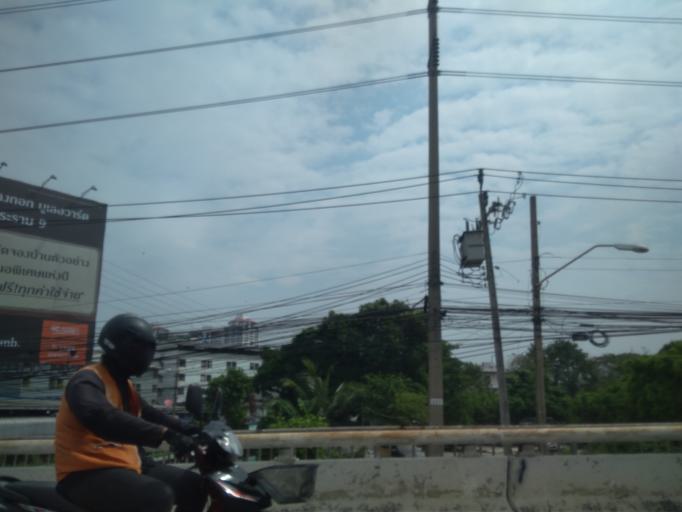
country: TH
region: Bangkok
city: Suan Luang
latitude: 13.7333
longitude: 100.6413
